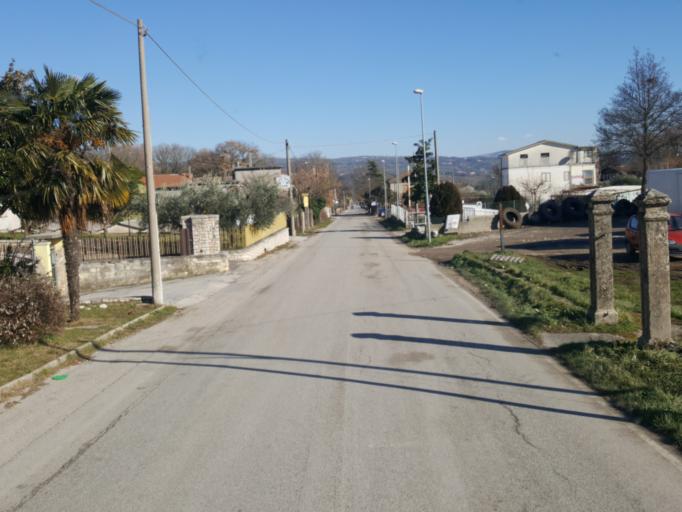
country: IT
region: Campania
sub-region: Provincia di Benevento
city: Morcone
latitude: 41.3426
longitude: 14.6780
